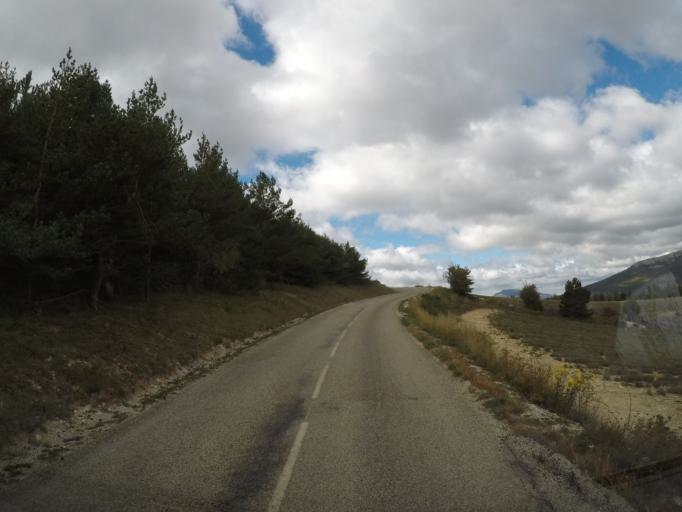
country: FR
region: Provence-Alpes-Cote d'Azur
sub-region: Departement du Vaucluse
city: Sault
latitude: 44.1741
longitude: 5.5064
